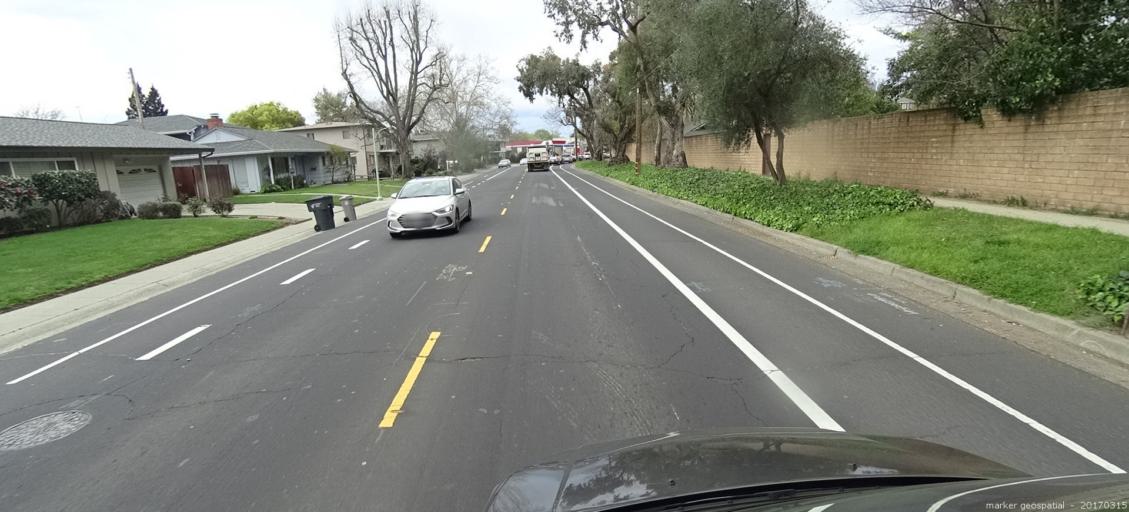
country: US
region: California
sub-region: Sacramento County
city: Sacramento
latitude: 38.5367
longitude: -121.5014
